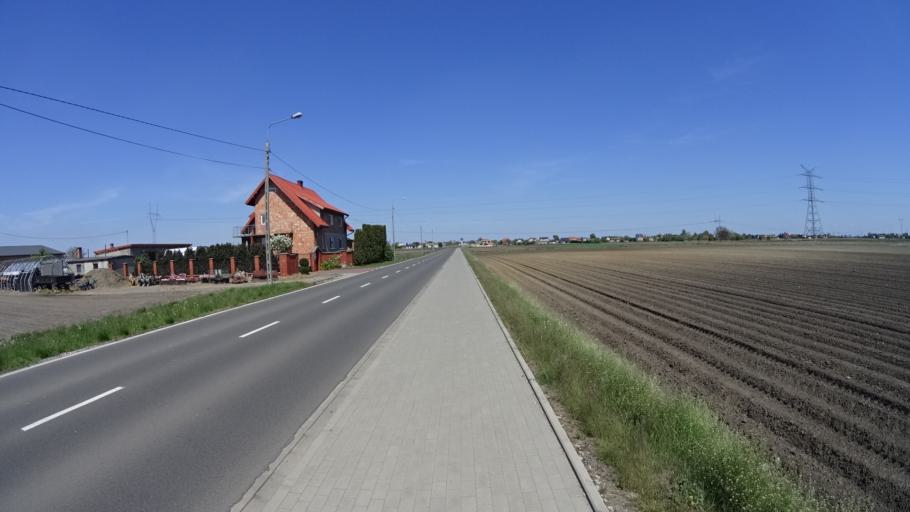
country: PL
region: Masovian Voivodeship
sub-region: Powiat warszawski zachodni
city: Jozefow
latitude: 52.2346
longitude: 20.7377
